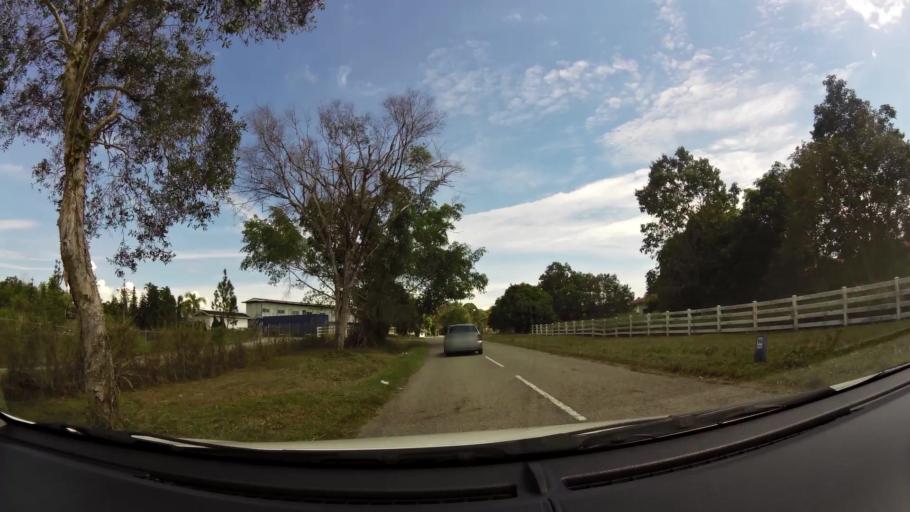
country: BN
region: Brunei and Muara
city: Bandar Seri Begawan
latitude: 4.9378
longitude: 114.8826
